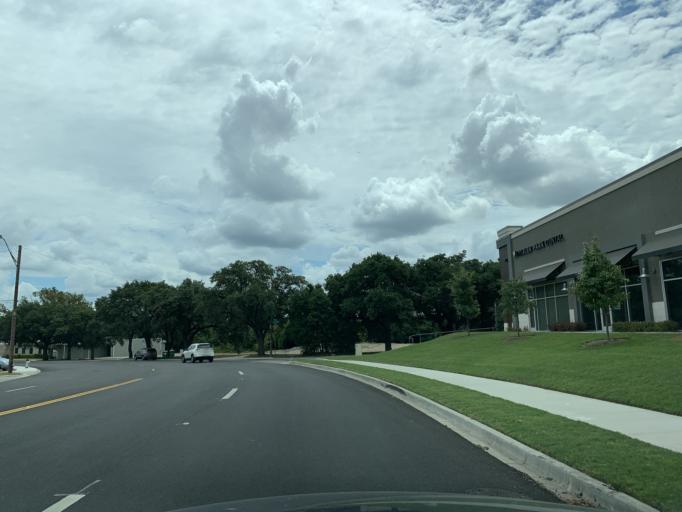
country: US
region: Texas
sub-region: Dallas County
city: Cockrell Hill
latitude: 32.7607
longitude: -96.8584
